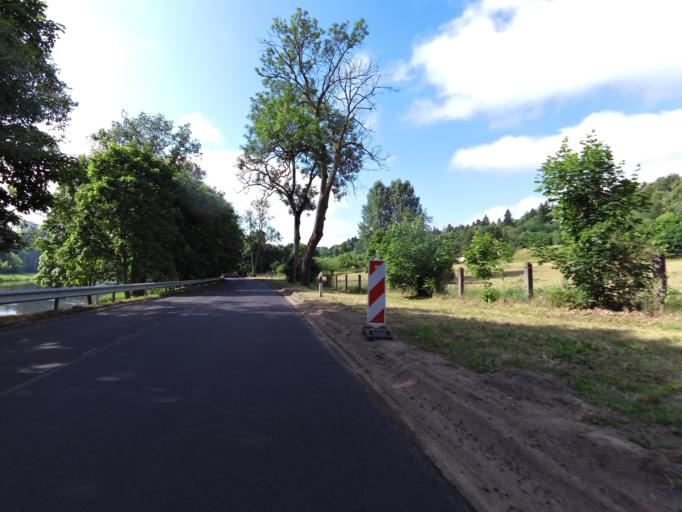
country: LT
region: Vilnius County
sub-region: Vilnius
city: Vilnius
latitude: 54.7336
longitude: 25.2903
